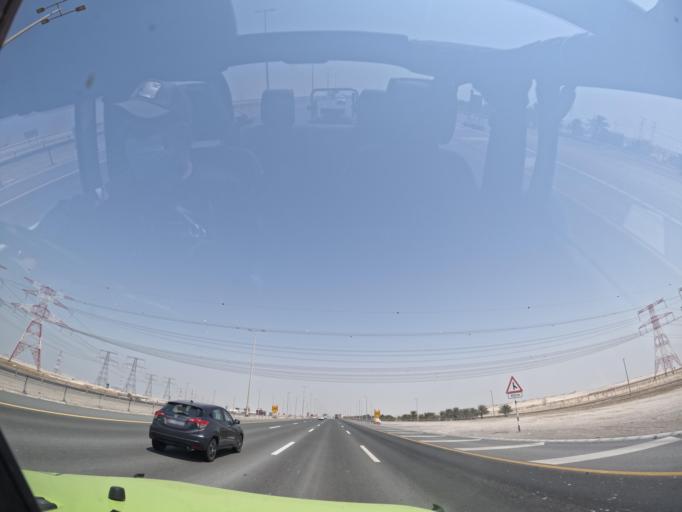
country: AE
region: Abu Dhabi
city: Abu Dhabi
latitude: 24.2194
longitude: 54.4292
